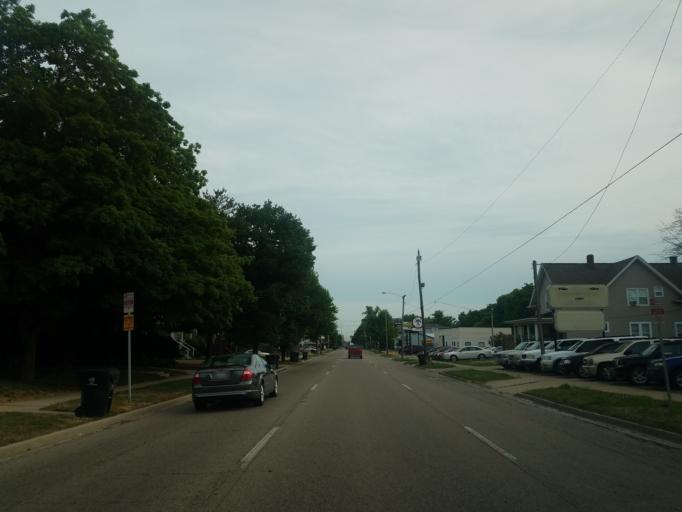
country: US
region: Illinois
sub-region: McLean County
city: Bloomington
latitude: 40.4667
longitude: -88.9931
